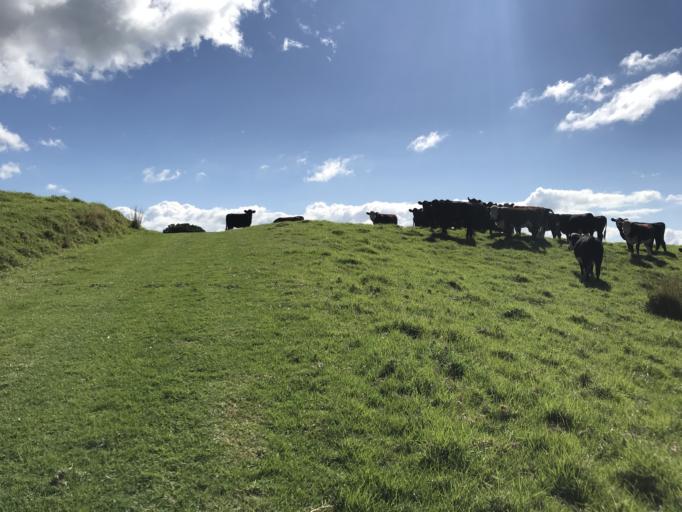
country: NZ
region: Auckland
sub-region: Auckland
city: Warkworth
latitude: -36.3766
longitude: 174.8375
